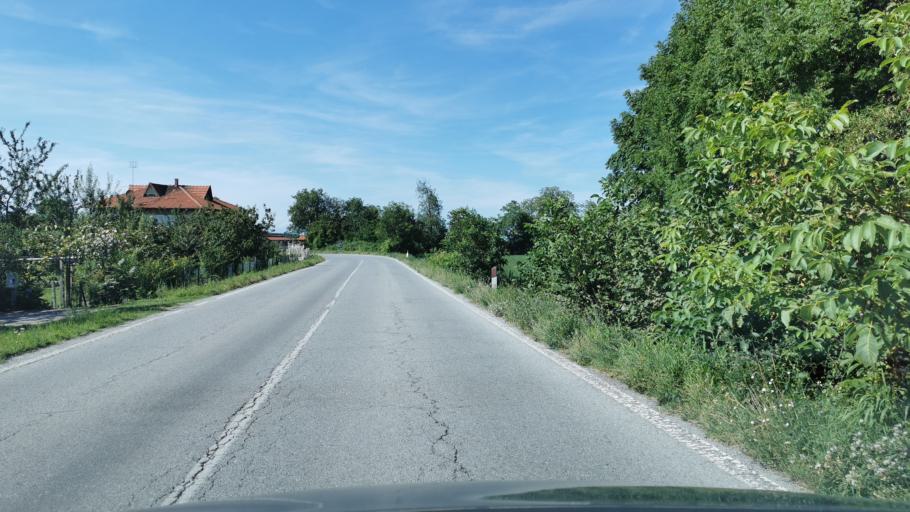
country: IT
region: Piedmont
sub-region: Provincia di Cuneo
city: Cuneo
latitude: 44.3732
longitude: 7.5590
